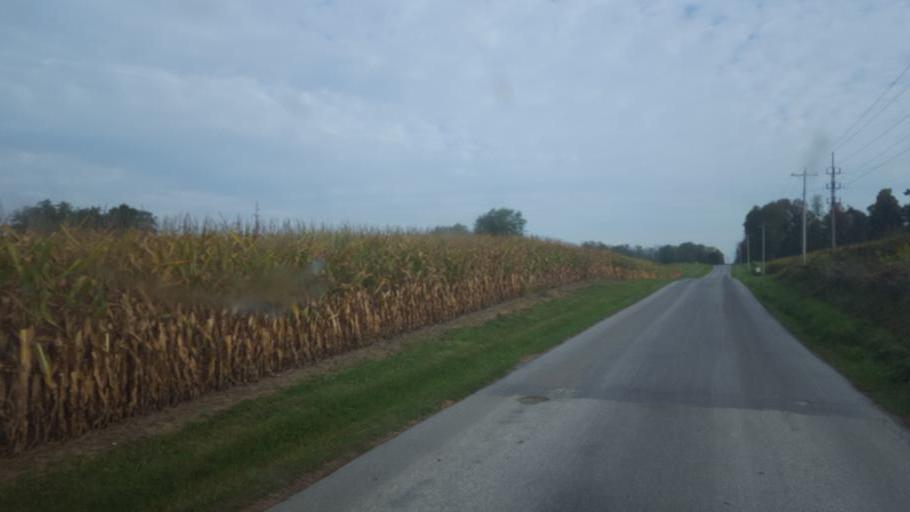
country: US
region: Ohio
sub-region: Knox County
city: Fredericktown
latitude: 40.5235
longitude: -82.6337
